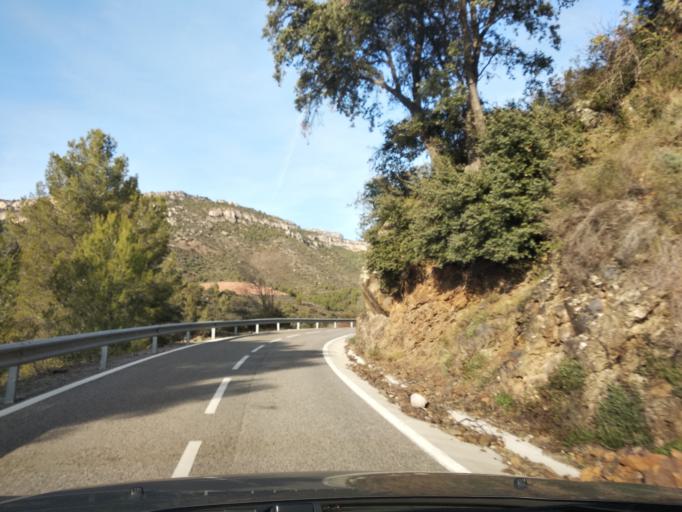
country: ES
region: Catalonia
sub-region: Provincia de Tarragona
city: Margalef
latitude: 41.2398
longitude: 0.7875
